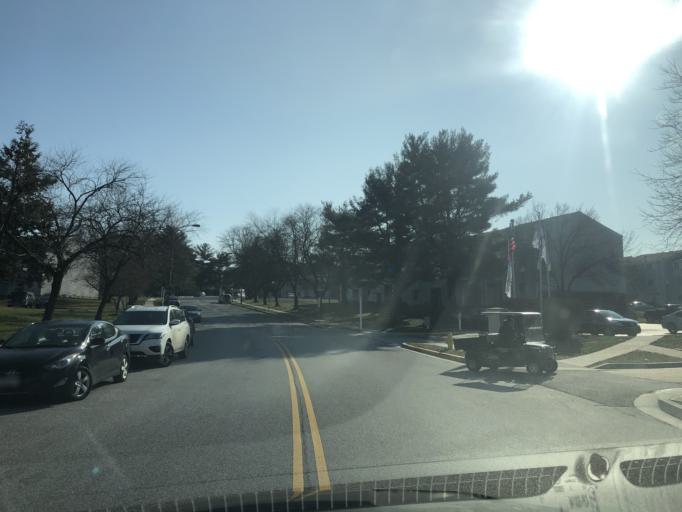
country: US
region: Maryland
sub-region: Anne Arundel County
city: Odenton
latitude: 39.0818
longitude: -76.6838
